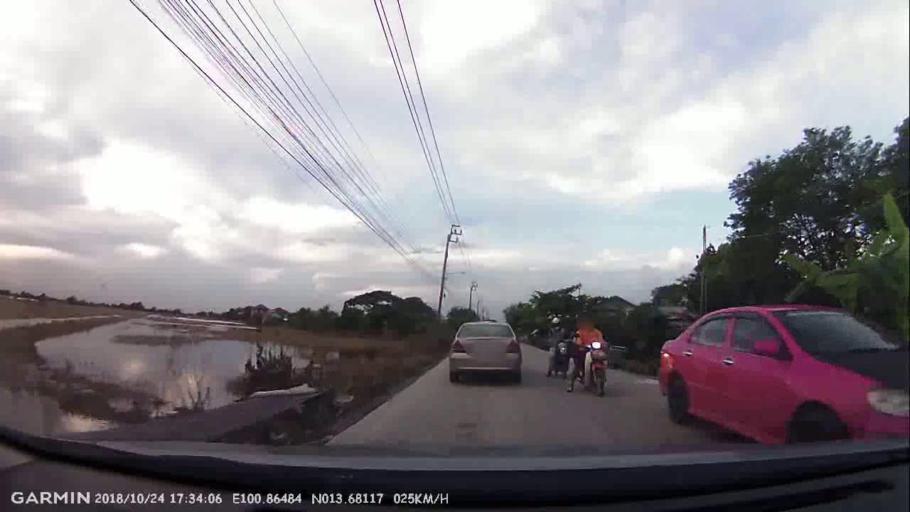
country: TH
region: Samut Prakan
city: Ban Khlong Bang Sao Thong
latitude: 13.6808
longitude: 100.8647
